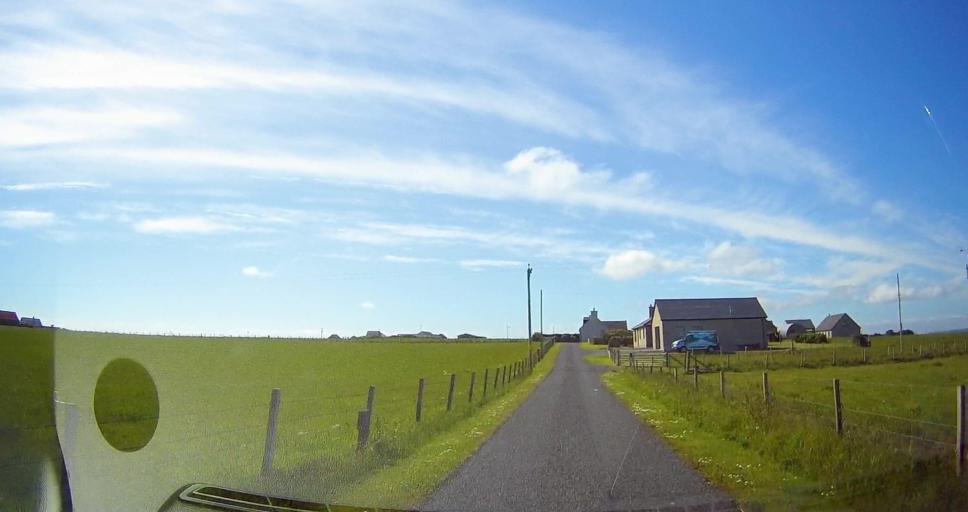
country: GB
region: Scotland
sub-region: Orkney Islands
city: Kirkwall
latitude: 58.8988
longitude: -2.9291
